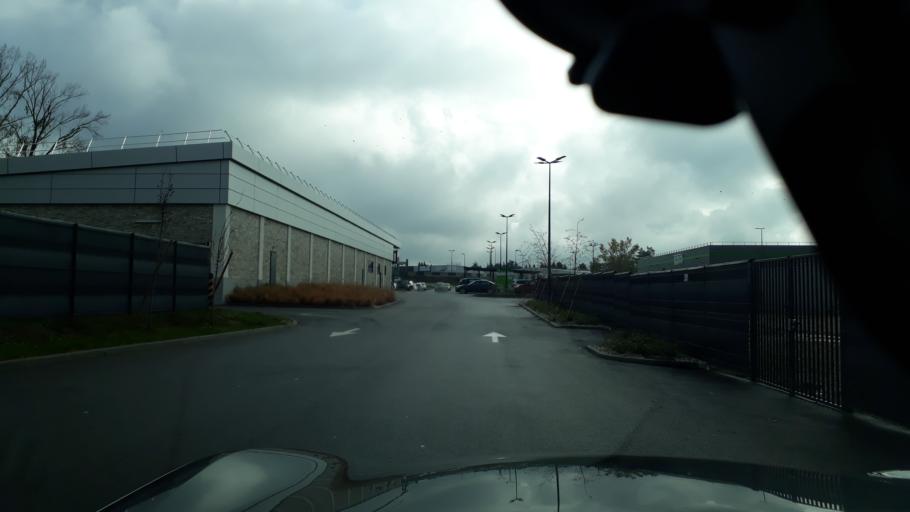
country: FR
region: Rhone-Alpes
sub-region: Departement de l'Ardeche
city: Davezieux
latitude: 45.2578
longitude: 4.6945
